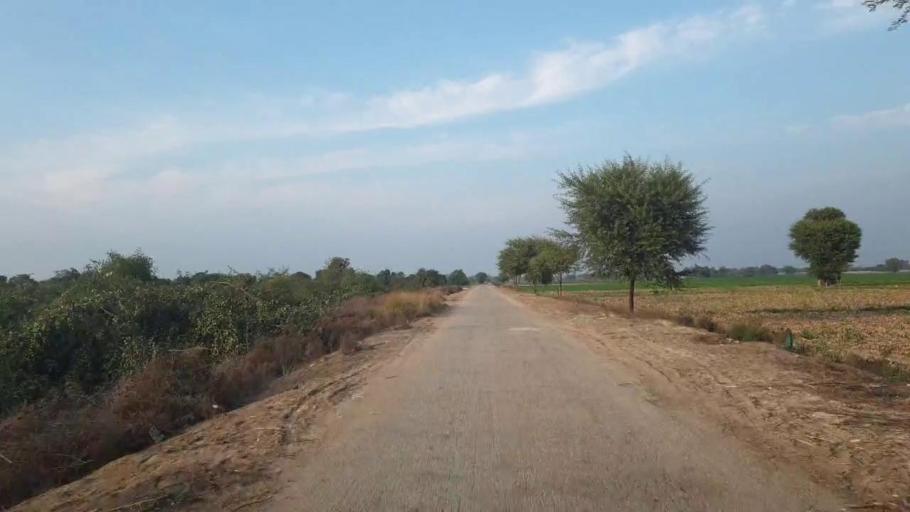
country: PK
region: Sindh
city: Shahpur Chakar
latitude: 26.1111
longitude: 68.5465
